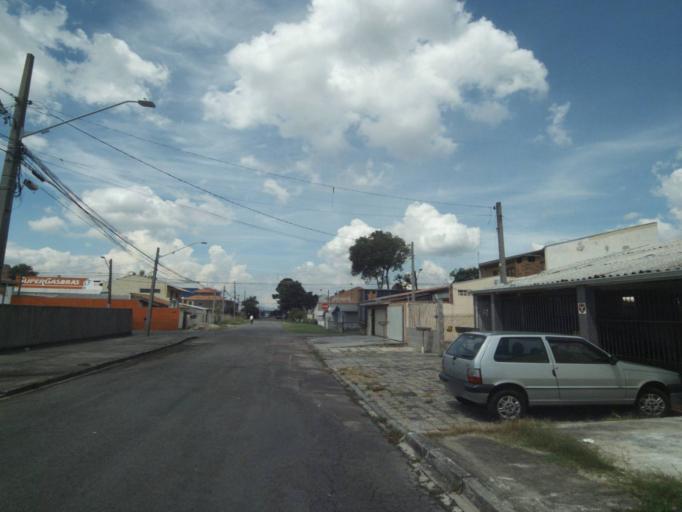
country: BR
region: Parana
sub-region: Pinhais
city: Pinhais
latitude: -25.4681
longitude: -49.2021
